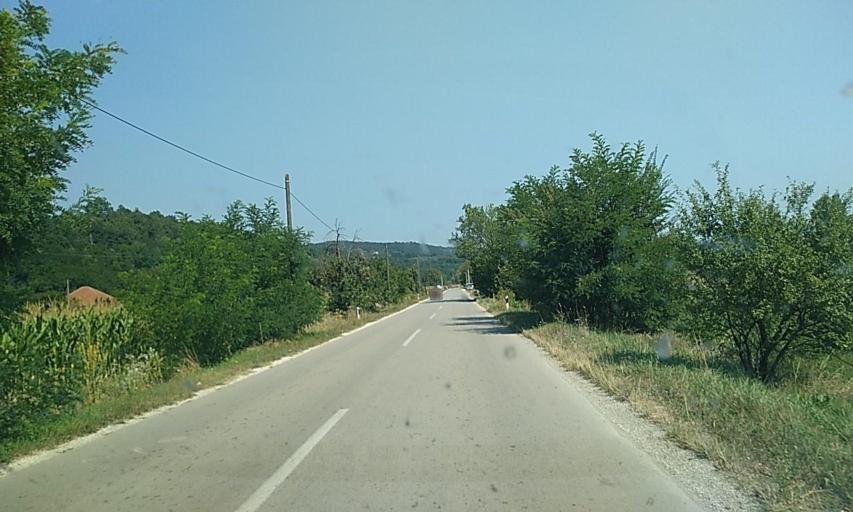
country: RS
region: Central Serbia
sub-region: Pcinjski Okrug
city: Vladicin Han
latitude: 42.6643
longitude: 22.0460
